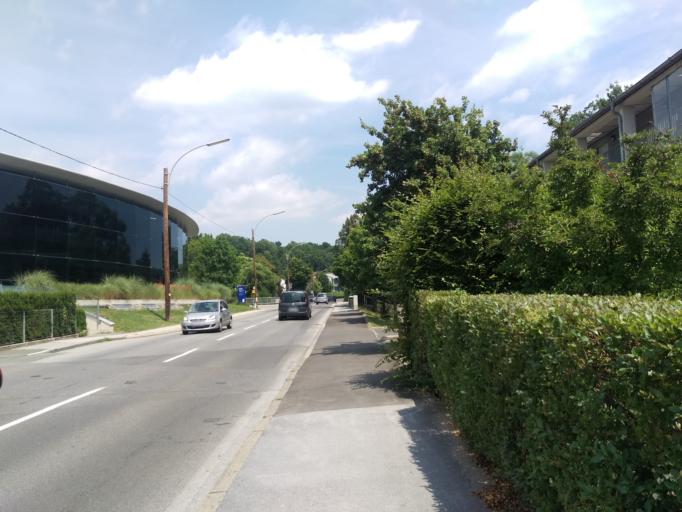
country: AT
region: Styria
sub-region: Graz Stadt
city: Mariatrost
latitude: 47.1008
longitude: 15.4795
